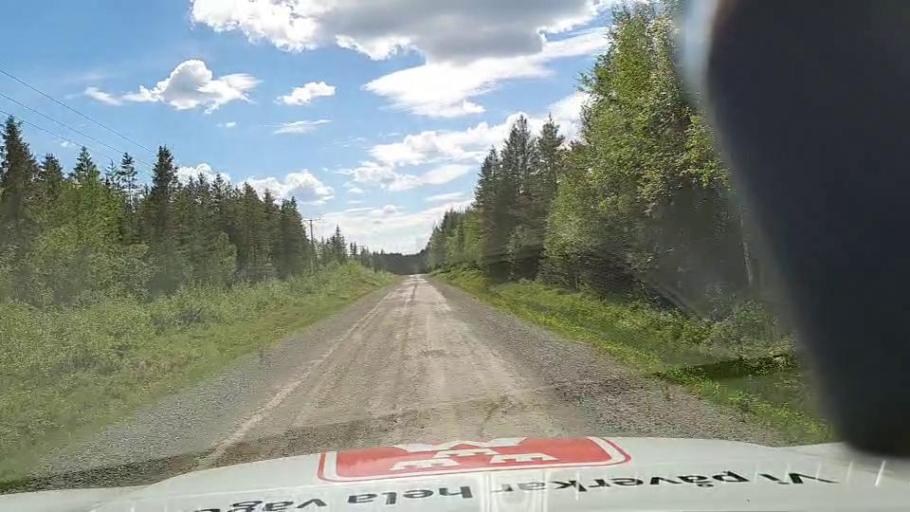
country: SE
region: Jaemtland
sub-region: Stroemsunds Kommun
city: Stroemsund
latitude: 64.5398
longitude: 15.6040
